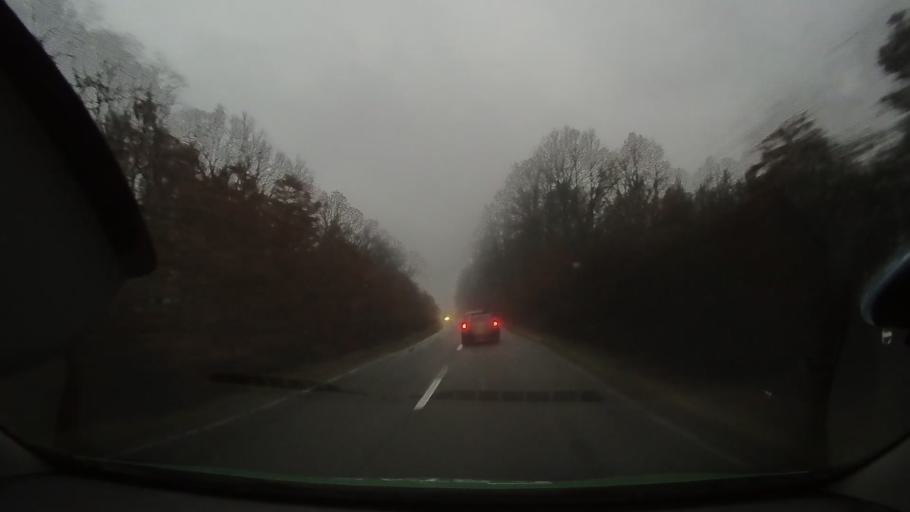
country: RO
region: Arad
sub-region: Comuna Beliu
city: Beliu
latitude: 46.5257
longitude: 21.9540
